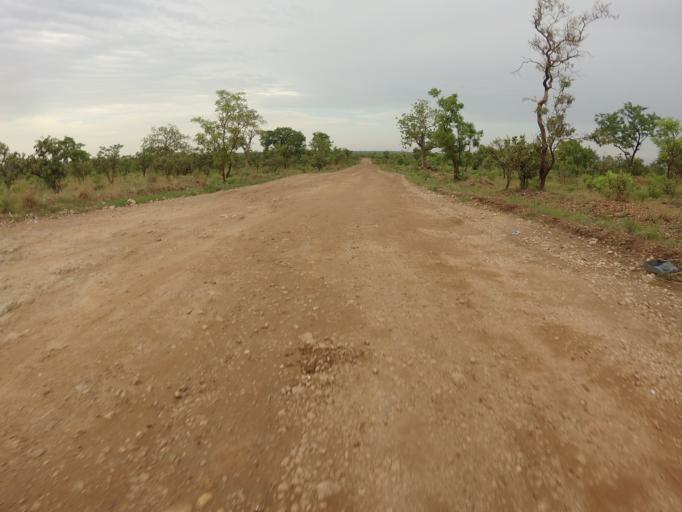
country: GH
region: Upper East
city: Bolgatanga
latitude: 10.8789
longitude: -0.6237
